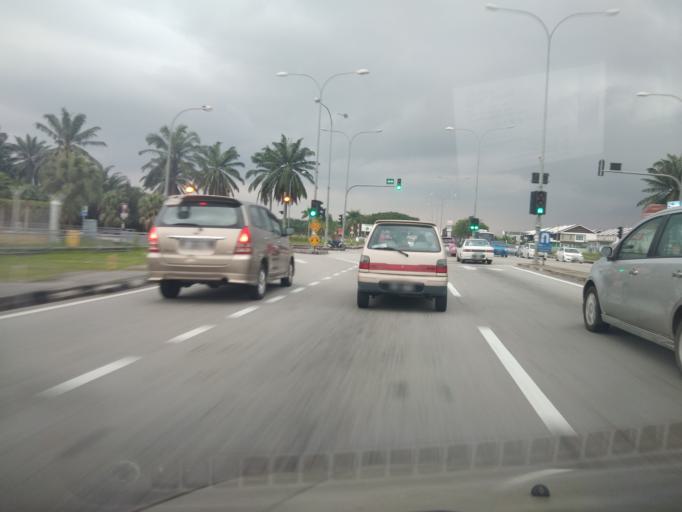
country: MY
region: Penang
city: Kepala Batas
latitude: 5.5194
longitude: 100.4700
